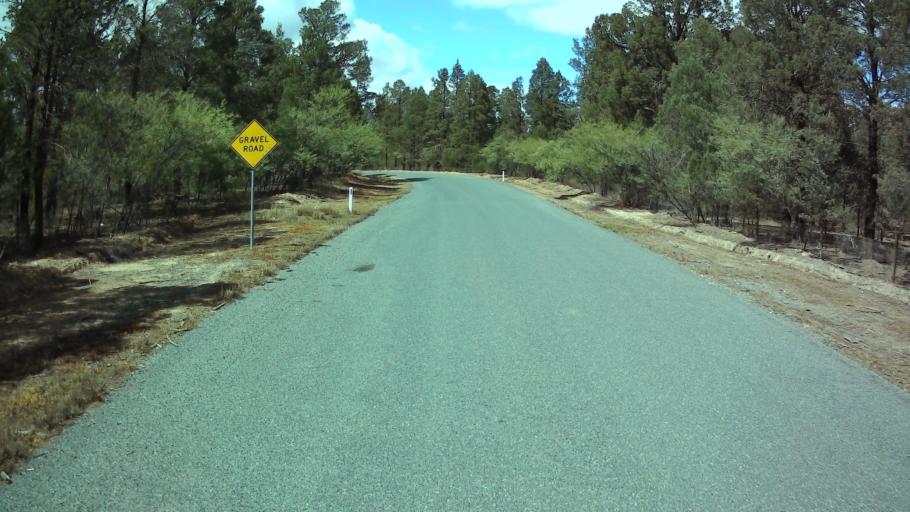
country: AU
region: New South Wales
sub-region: Weddin
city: Grenfell
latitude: -33.9087
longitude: 147.9193
